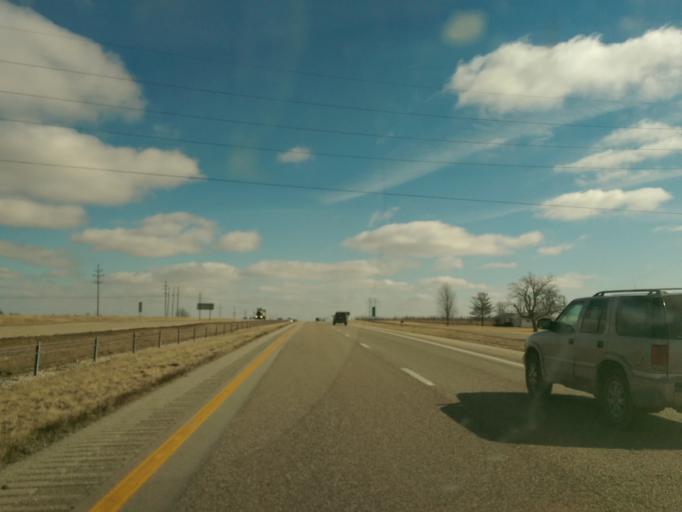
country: US
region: Missouri
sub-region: Montgomery County
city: Montgomery City
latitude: 38.8945
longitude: -91.4386
